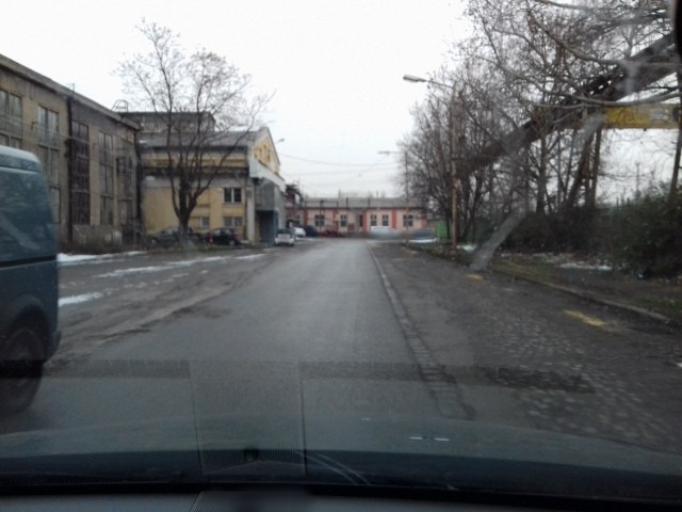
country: HU
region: Budapest
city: Budapest XXI. keruelet
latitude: 47.4340
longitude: 19.0618
